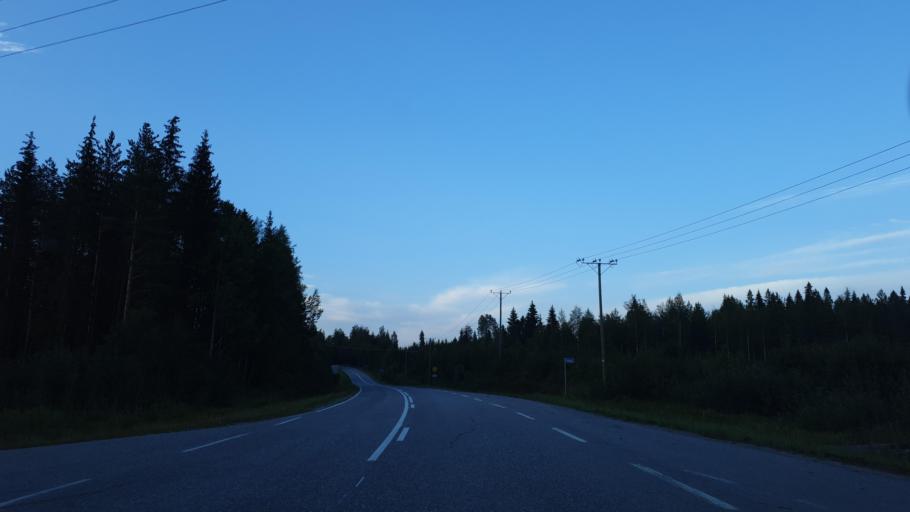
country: FI
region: Northern Savo
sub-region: Koillis-Savo
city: Kaavi
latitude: 62.9675
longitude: 28.7660
